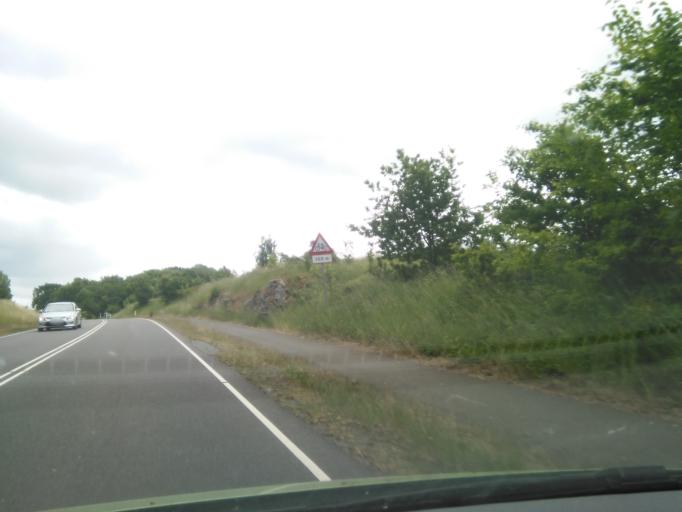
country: DK
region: Capital Region
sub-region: Bornholm Kommune
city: Akirkeby
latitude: 55.2237
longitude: 14.8911
